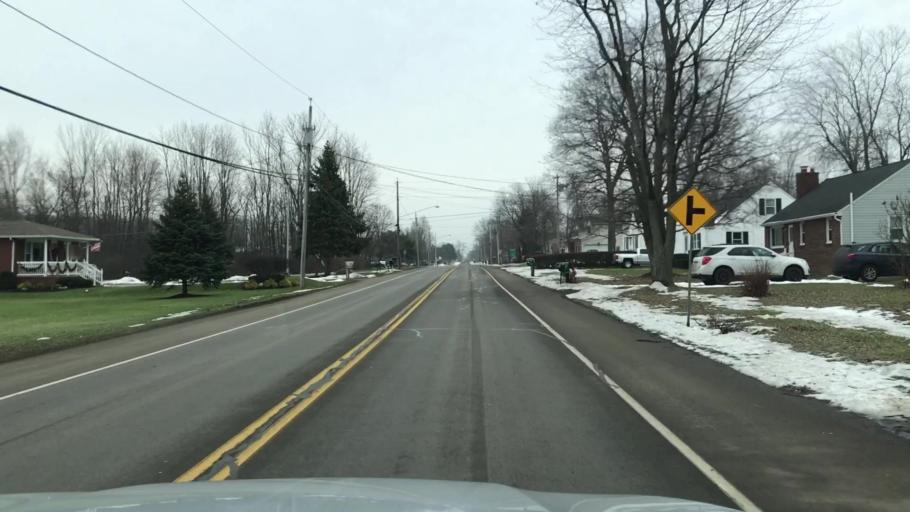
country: US
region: New York
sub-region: Erie County
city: Hamburg
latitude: 42.7514
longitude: -78.8430
